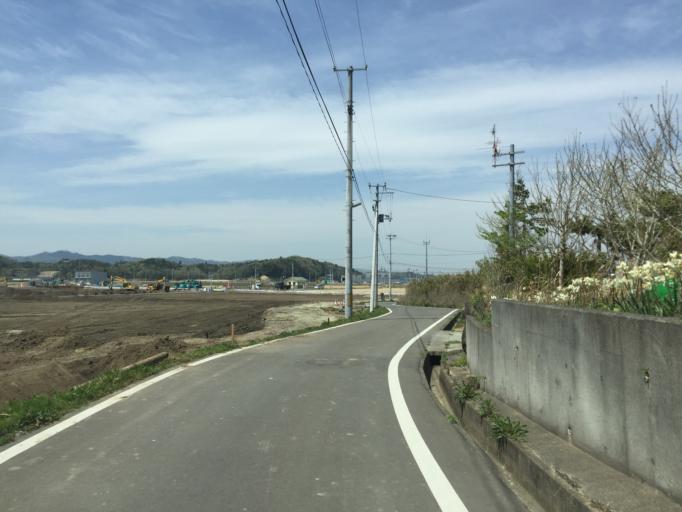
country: JP
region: Miyagi
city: Watari
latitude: 37.8987
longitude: 140.9261
